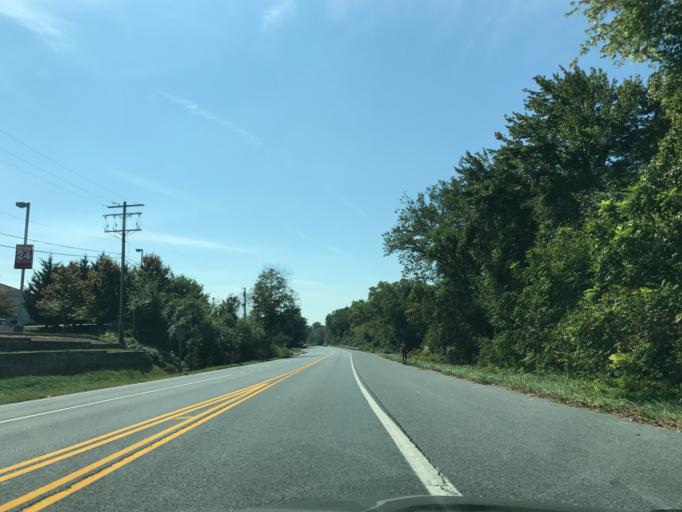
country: US
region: Maryland
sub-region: Anne Arundel County
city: Jessup
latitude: 39.1929
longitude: -76.7946
